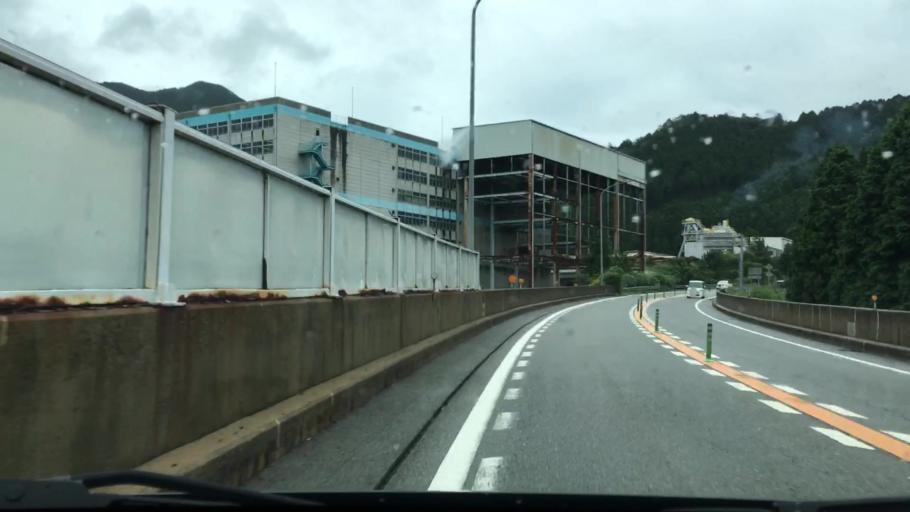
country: JP
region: Hyogo
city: Nishiwaki
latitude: 35.1490
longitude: 134.7877
